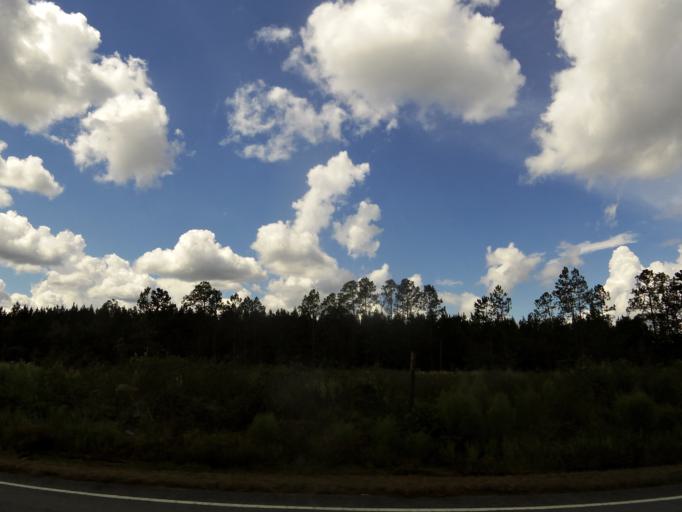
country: US
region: Georgia
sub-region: Brantley County
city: Nahunta
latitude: 31.0347
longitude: -82.0210
